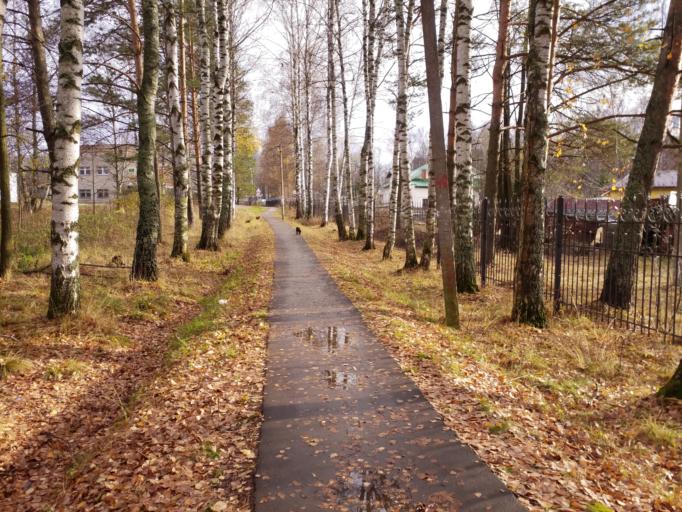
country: RU
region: Moskovskaya
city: Ashukino
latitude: 56.1629
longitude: 37.9430
